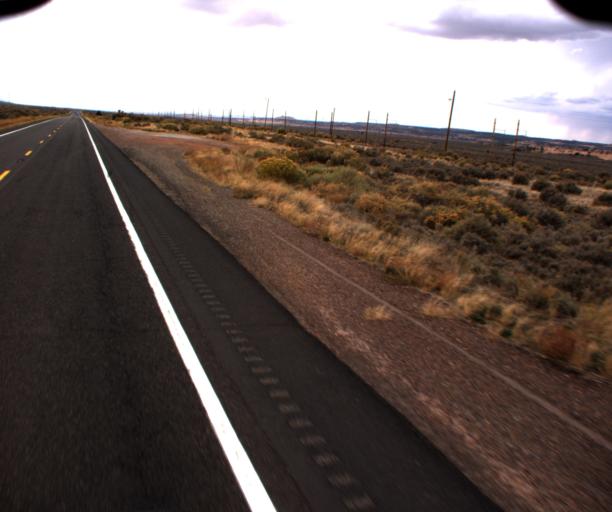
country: US
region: Arizona
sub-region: Navajo County
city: Kayenta
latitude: 36.5502
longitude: -110.5278
